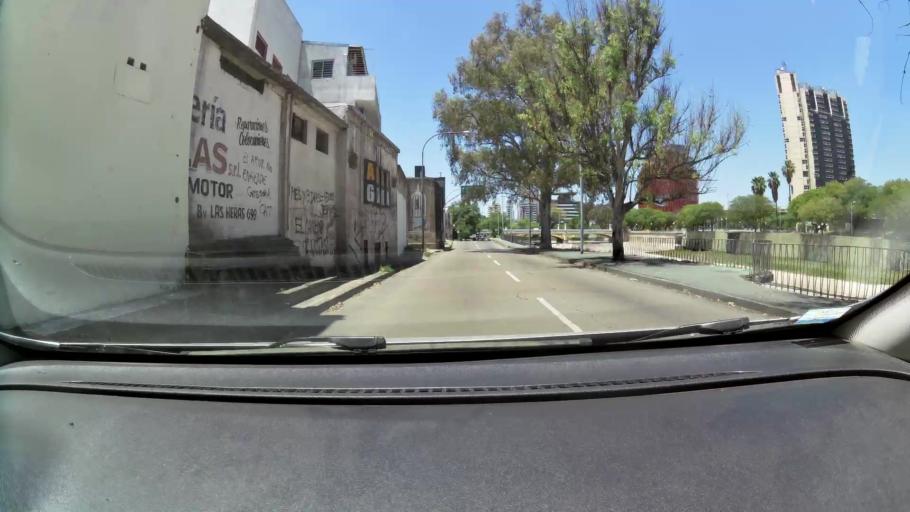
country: AR
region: Cordoba
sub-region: Departamento de Capital
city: Cordoba
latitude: -31.4058
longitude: -64.1899
